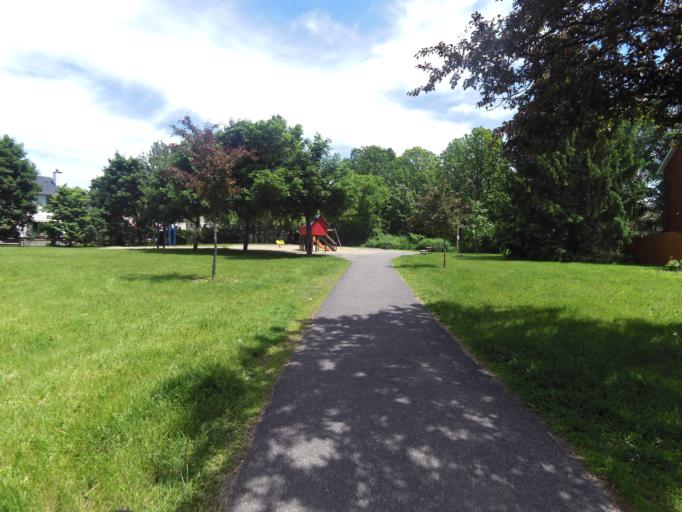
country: CA
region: Ontario
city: Ottawa
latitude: 45.3741
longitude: -75.6142
